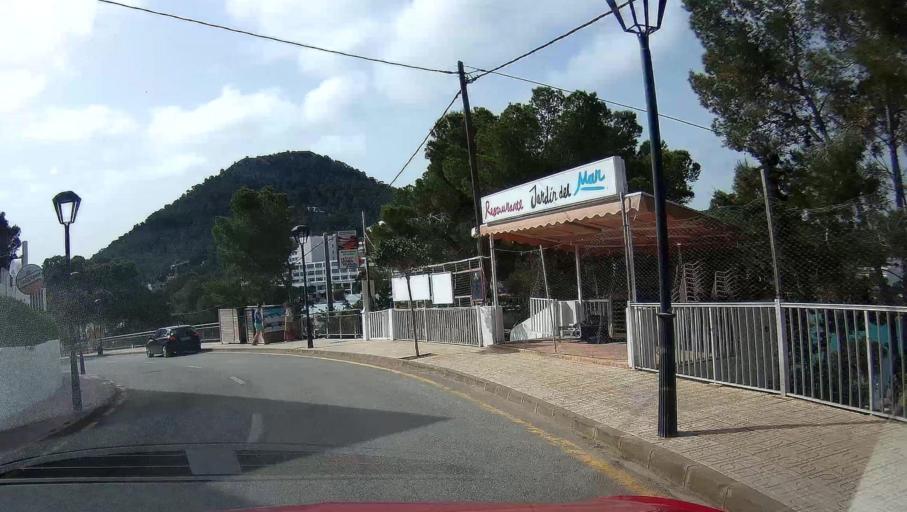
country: ES
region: Balearic Islands
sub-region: Illes Balears
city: Sant Joan de Labritja
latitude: 39.1113
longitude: 1.5170
